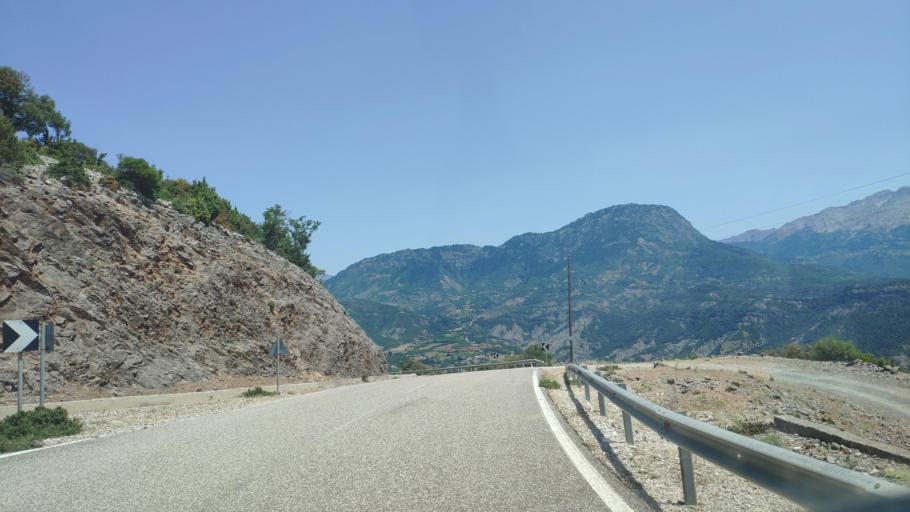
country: GR
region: Central Greece
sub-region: Nomos Evrytanias
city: Kerasochori
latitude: 39.0931
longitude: 21.4115
